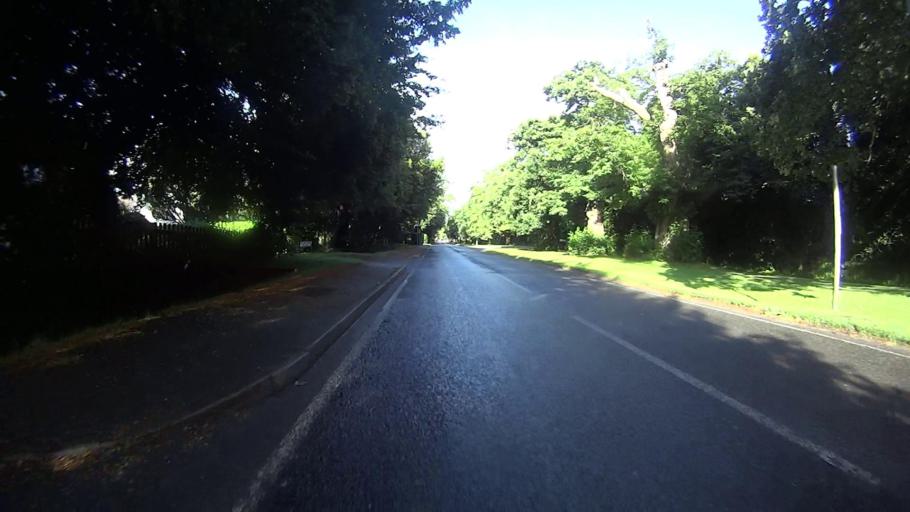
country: GB
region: England
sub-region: Surrey
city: Felbridge
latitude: 51.1388
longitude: -0.0484
